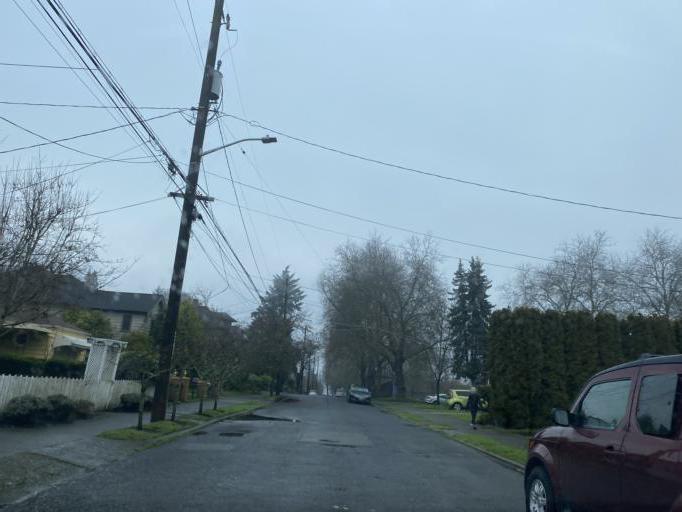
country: US
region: Washington
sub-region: King County
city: Seattle
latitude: 47.6098
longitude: -122.2905
